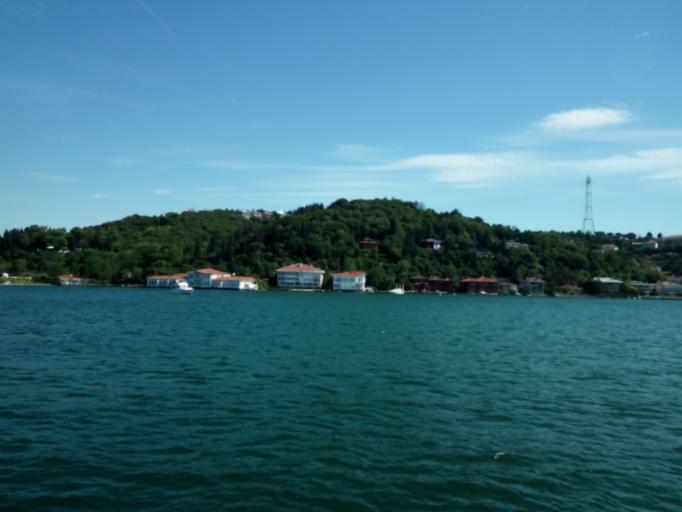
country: TR
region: Istanbul
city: UEskuedar
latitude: 41.0791
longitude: 29.0607
